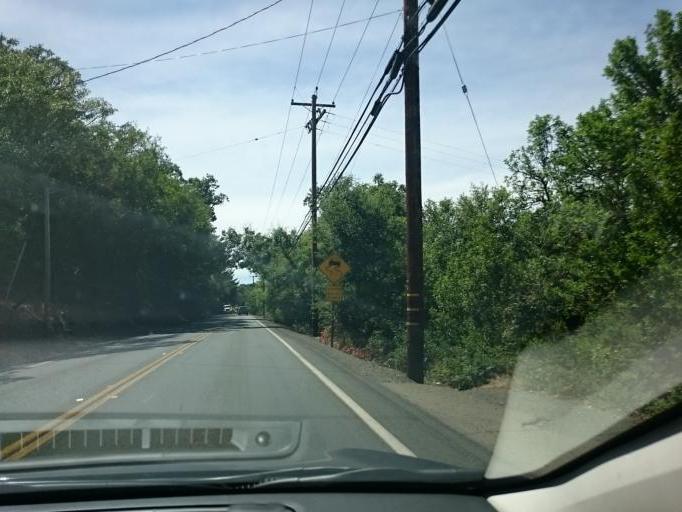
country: US
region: California
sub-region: Sonoma County
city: Healdsburg
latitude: 38.6590
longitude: -122.8374
